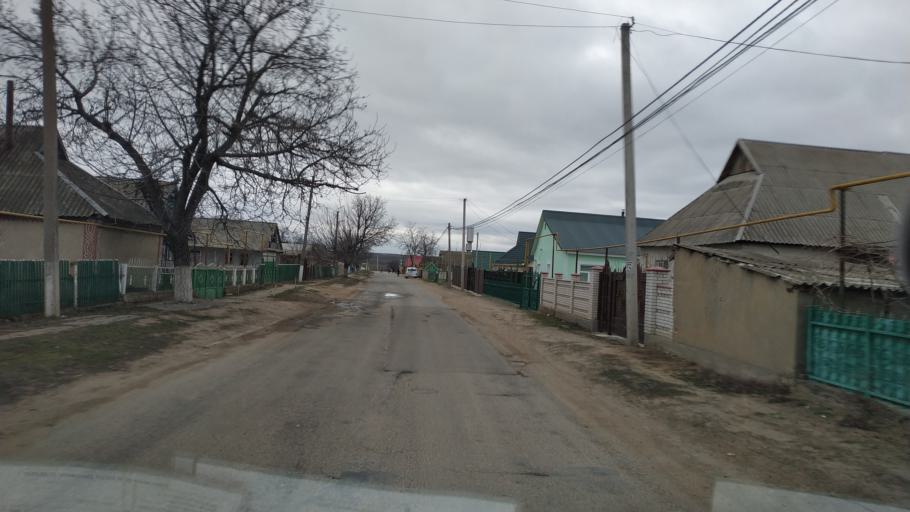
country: MD
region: Causeni
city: Causeni
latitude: 46.6658
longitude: 29.4848
